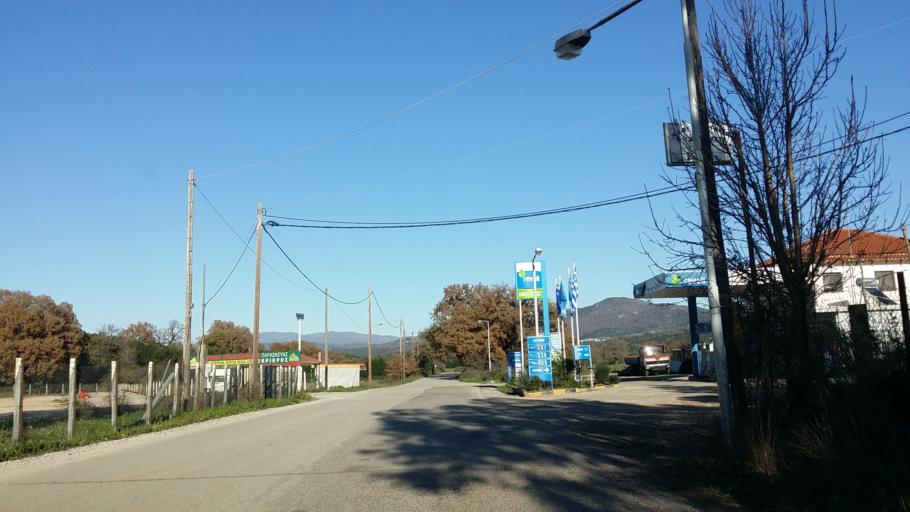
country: GR
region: West Greece
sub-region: Nomos Aitolias kai Akarnanias
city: Fitiai
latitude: 38.6175
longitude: 21.1439
